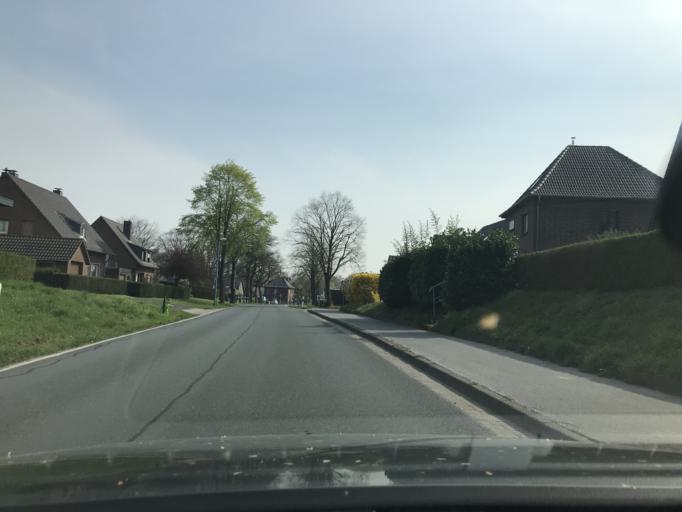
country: DE
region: North Rhine-Westphalia
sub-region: Regierungsbezirk Dusseldorf
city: Kleve
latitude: 51.7626
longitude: 6.1720
